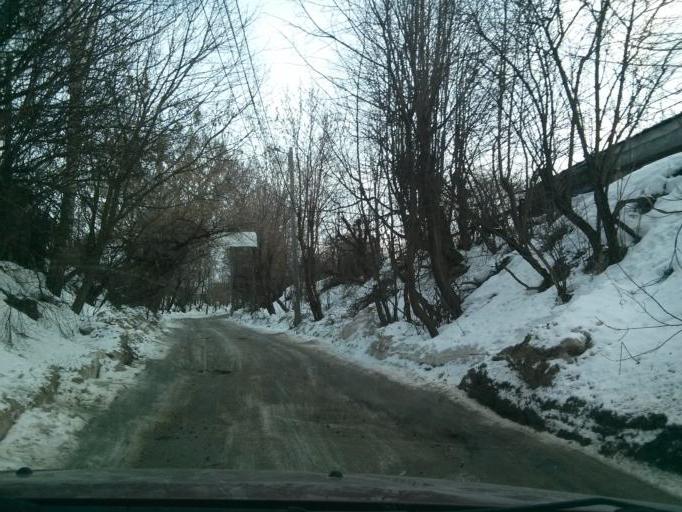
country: RU
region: Nizjnij Novgorod
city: Nizhniy Novgorod
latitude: 56.2743
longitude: 44.0324
